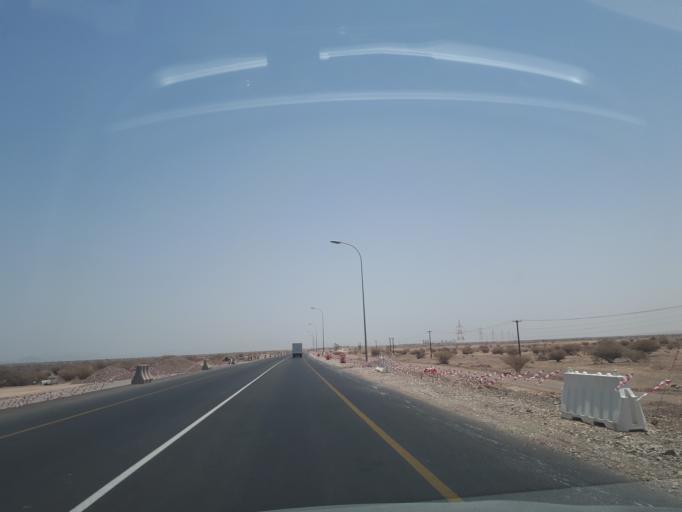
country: OM
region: Ash Sharqiyah
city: Badiyah
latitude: 22.4175
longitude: 59.0500
